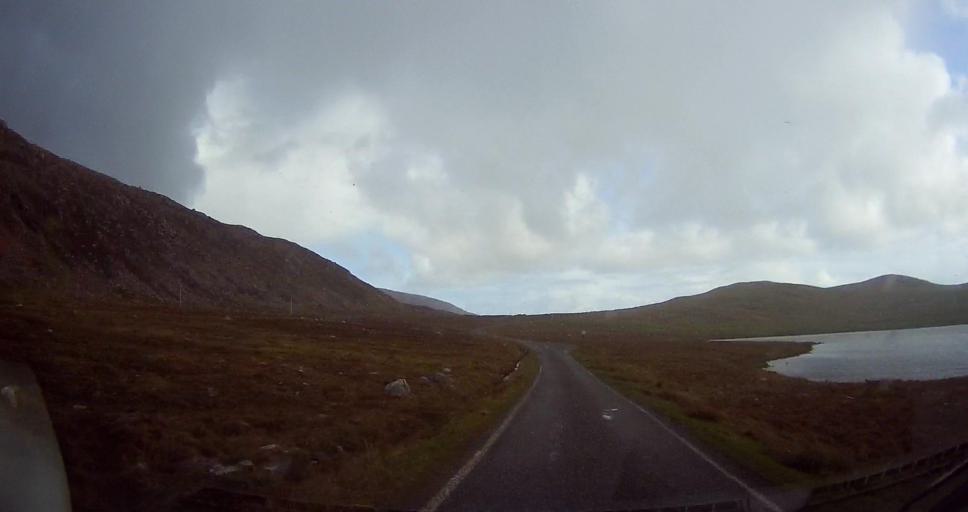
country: GB
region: Scotland
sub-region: Shetland Islands
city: Lerwick
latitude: 60.5494
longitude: -1.3409
